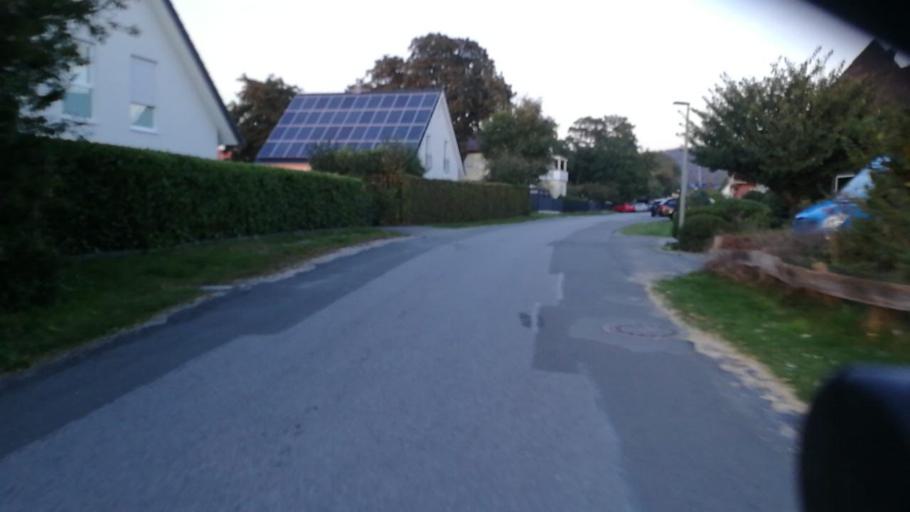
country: DE
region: North Rhine-Westphalia
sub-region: Regierungsbezirk Detmold
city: Steinhagen
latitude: 52.0198
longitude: 8.4111
